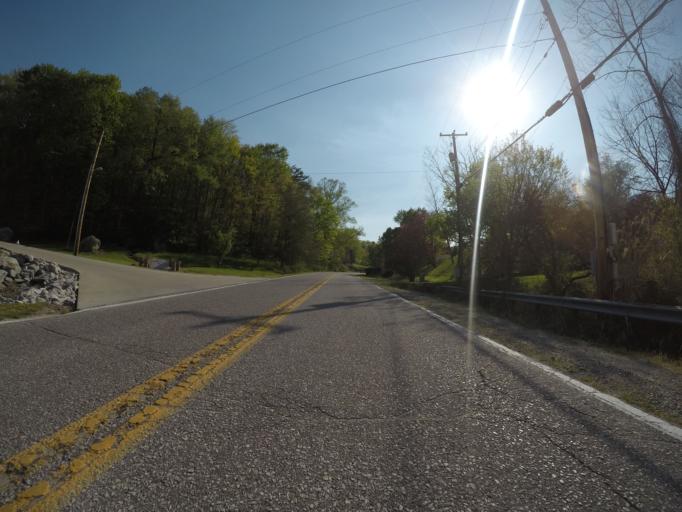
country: US
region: West Virginia
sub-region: Kanawha County
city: Charleston
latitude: 38.3844
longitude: -81.6015
